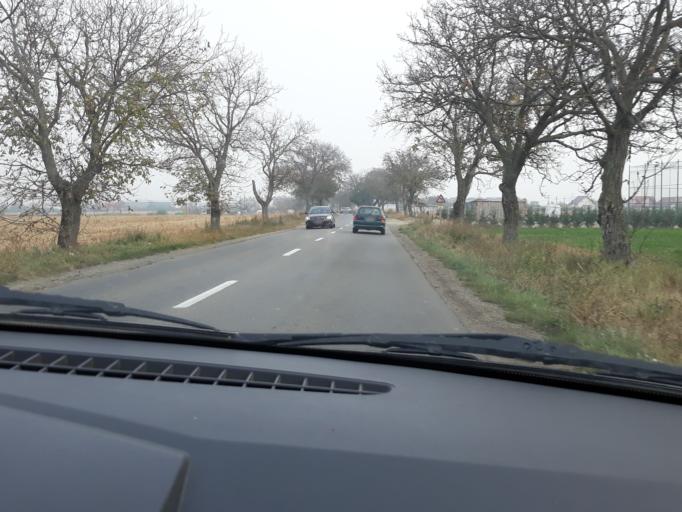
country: RO
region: Bihor
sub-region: Comuna Santandrei
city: Santandrei
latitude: 47.0525
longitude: 21.8751
